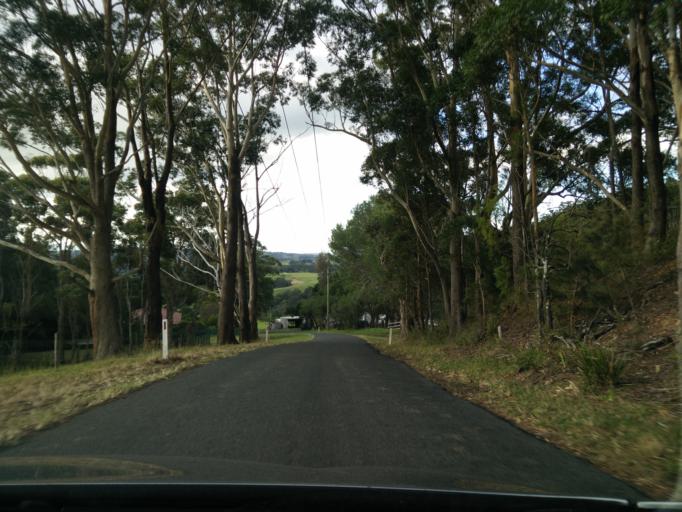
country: AU
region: New South Wales
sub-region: Kiama
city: Jamberoo
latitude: -34.6745
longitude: 150.7929
